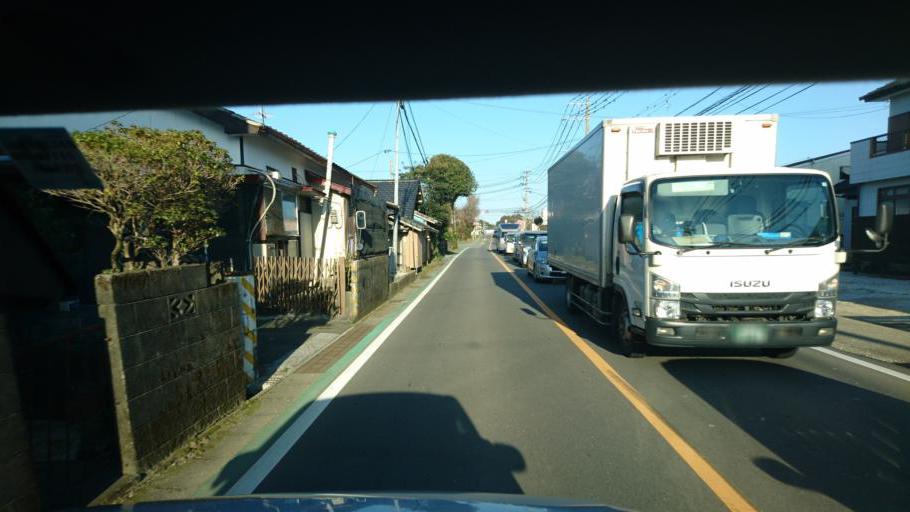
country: JP
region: Miyazaki
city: Miyazaki-shi
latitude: 31.8465
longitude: 131.3928
